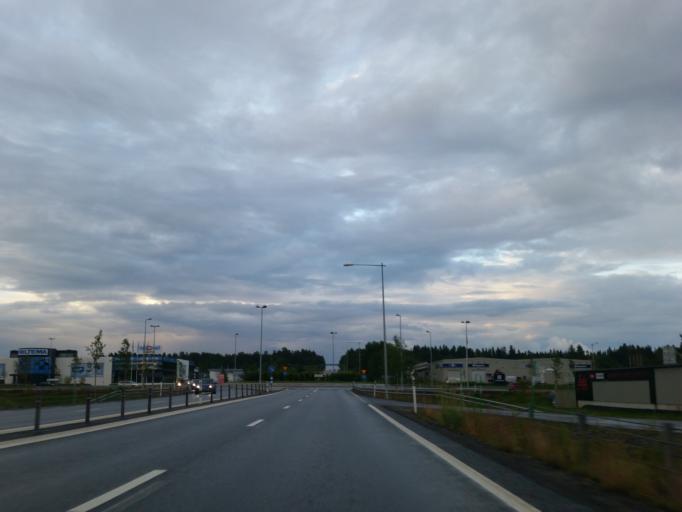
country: SE
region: Vaesterbotten
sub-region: Umea Kommun
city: Ersmark
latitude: 63.8485
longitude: 20.3114
